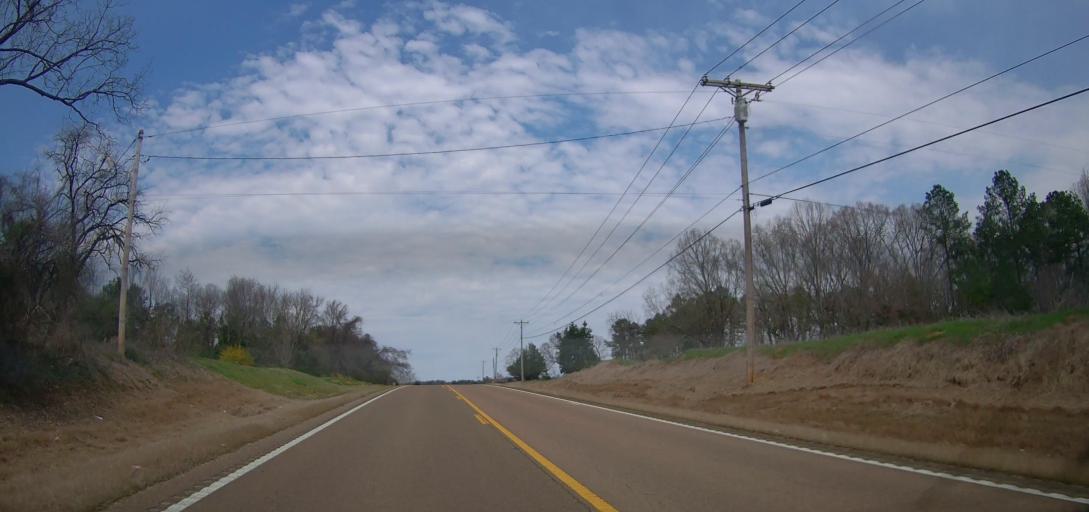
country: US
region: Mississippi
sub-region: Marshall County
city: Holly Springs
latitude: 34.7371
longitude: -89.4233
